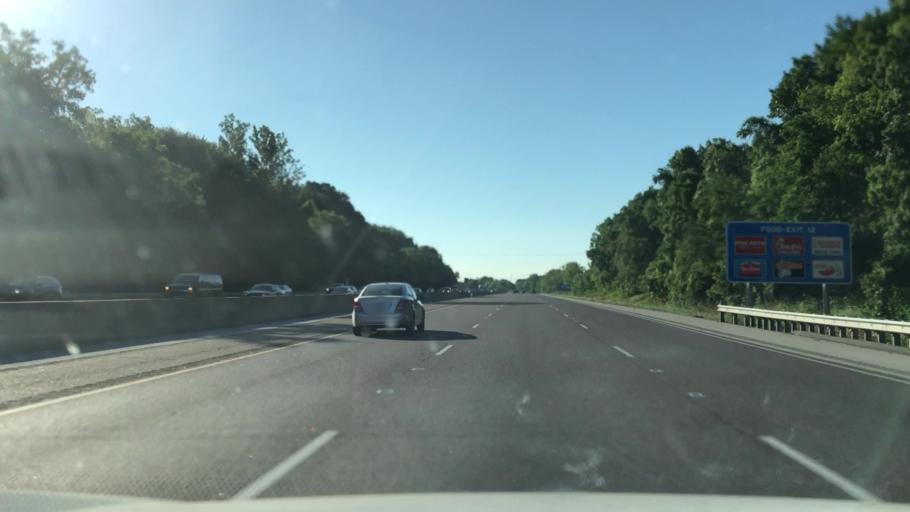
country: US
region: Illinois
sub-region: Saint Clair County
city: Caseyville
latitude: 38.6046
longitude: -90.0244
